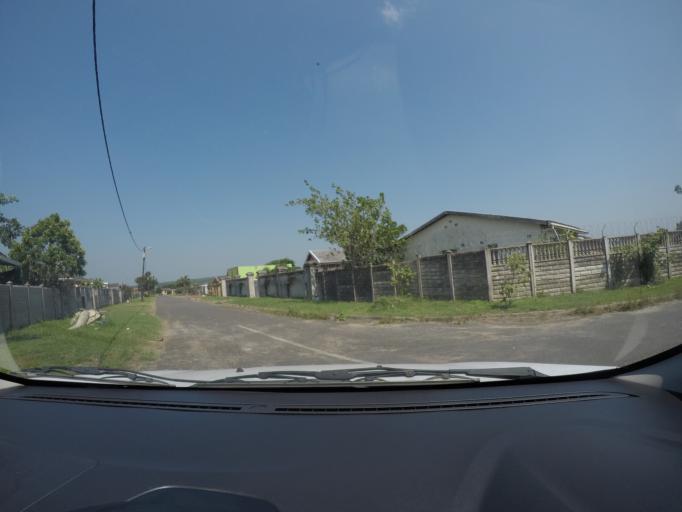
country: ZA
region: KwaZulu-Natal
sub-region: uThungulu District Municipality
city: eSikhawini
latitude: -28.8665
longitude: 31.9169
